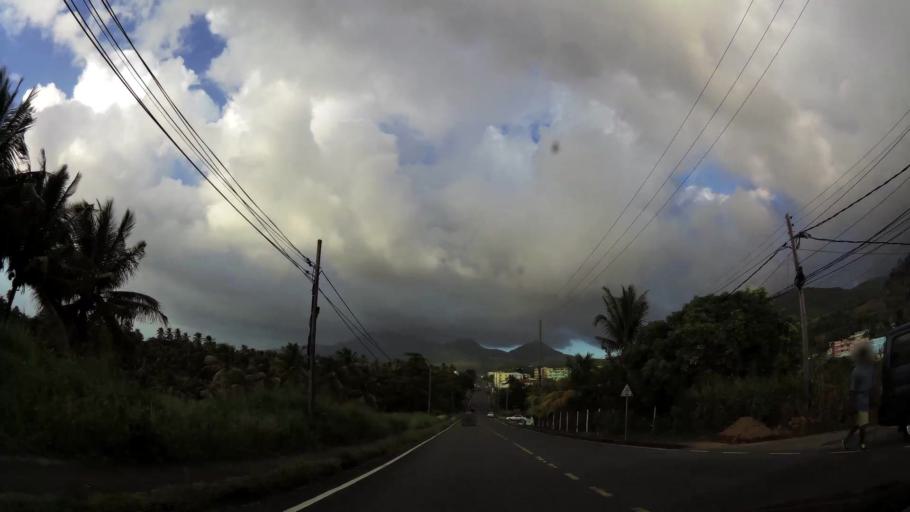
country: DM
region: Saint John
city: Portsmouth
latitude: 15.5510
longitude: -61.4621
